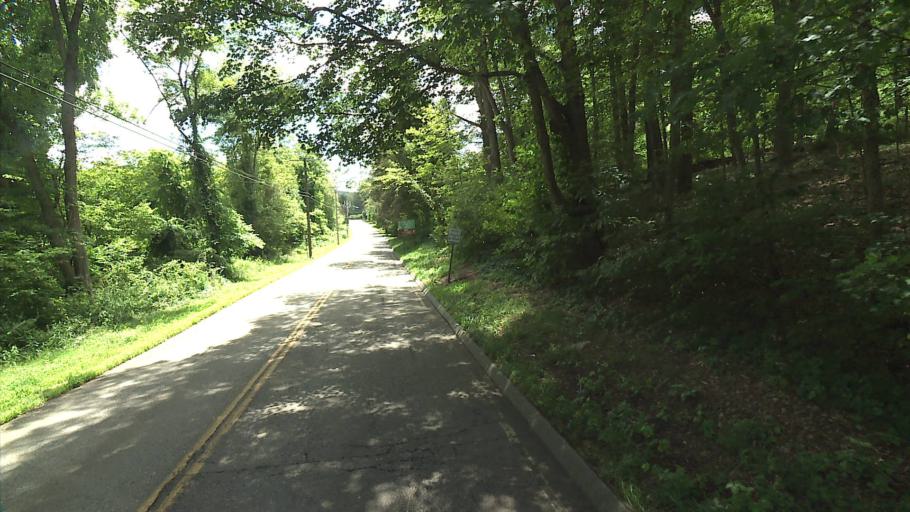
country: US
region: Connecticut
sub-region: Middlesex County
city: East Hampton
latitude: 41.5605
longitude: -72.5549
